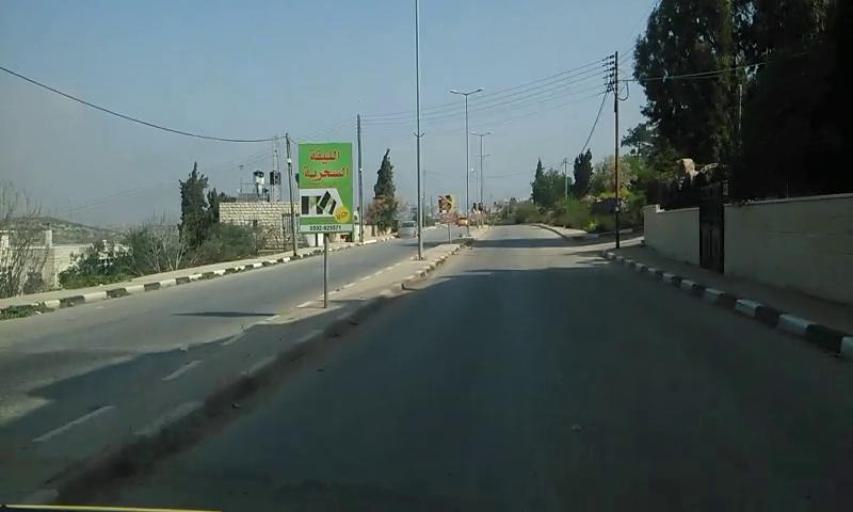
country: PS
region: West Bank
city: `Ayn Yabrud
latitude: 31.9559
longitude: 35.2529
